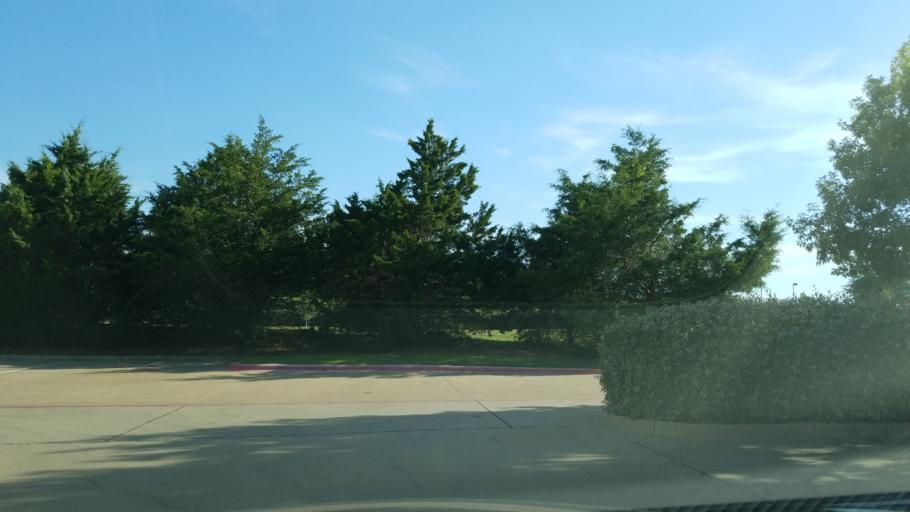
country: US
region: Texas
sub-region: Dallas County
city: Coppell
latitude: 32.8877
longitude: -96.9752
